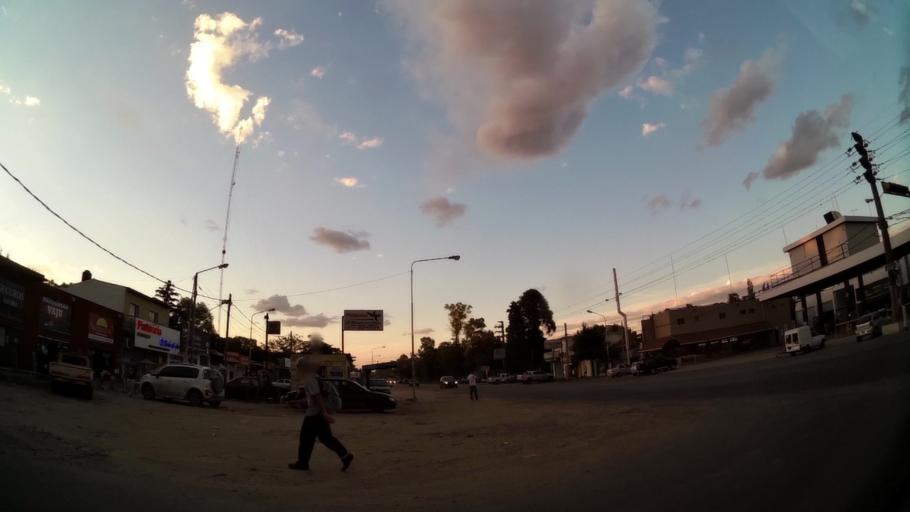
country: AR
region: Buenos Aires
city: Santa Catalina - Dique Lujan
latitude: -34.4825
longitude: -58.7775
